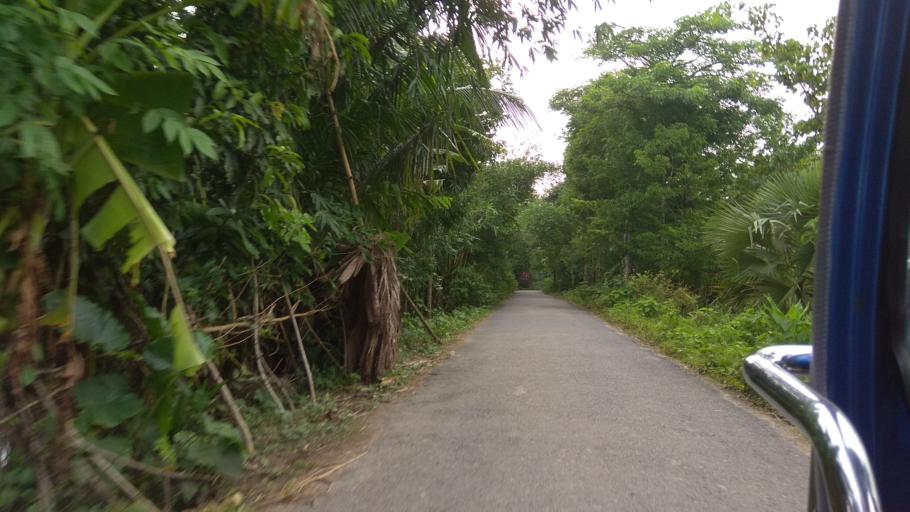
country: BD
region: Khulna
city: Kalia
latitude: 23.0375
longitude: 89.6705
